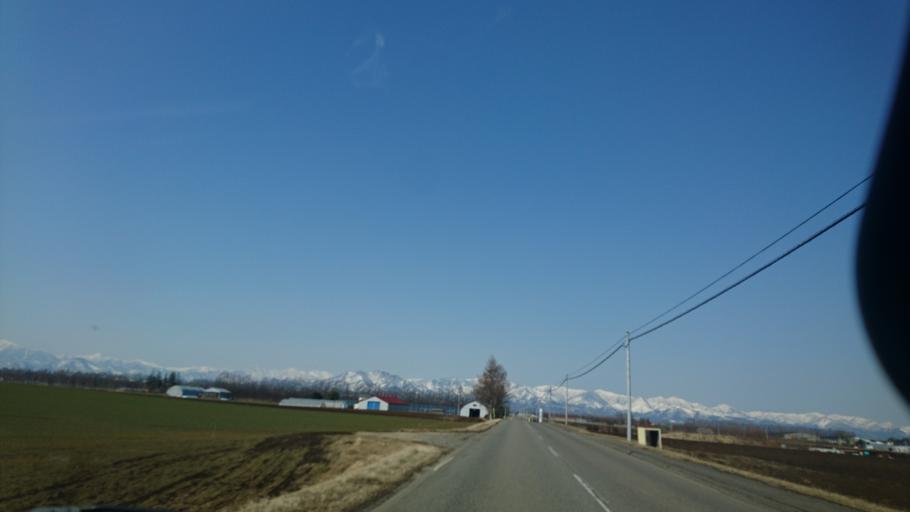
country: JP
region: Hokkaido
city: Obihiro
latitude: 42.9043
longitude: 143.0977
